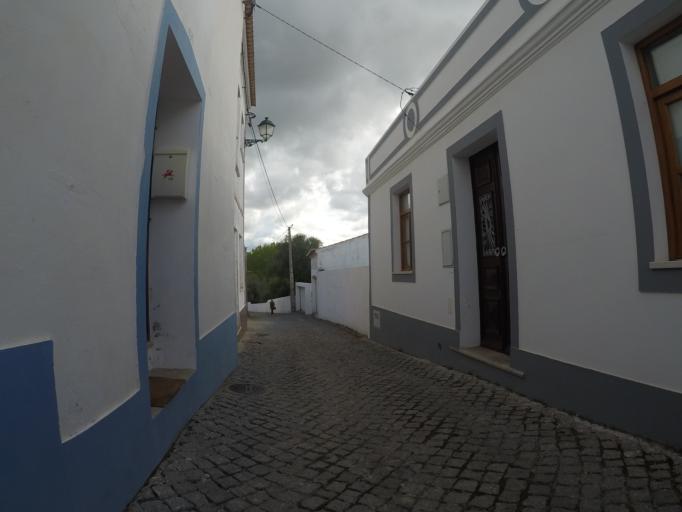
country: PT
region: Faro
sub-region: Aljezur
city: Aljezur
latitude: 37.3195
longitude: -8.8027
